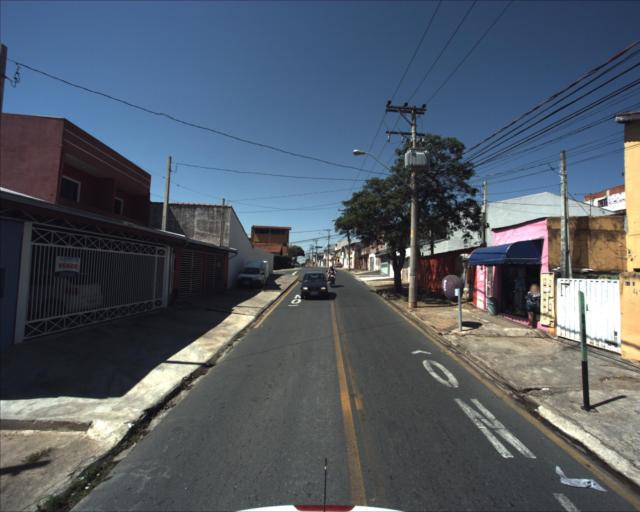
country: BR
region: Sao Paulo
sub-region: Sorocaba
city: Sorocaba
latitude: -23.4651
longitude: -47.4838
